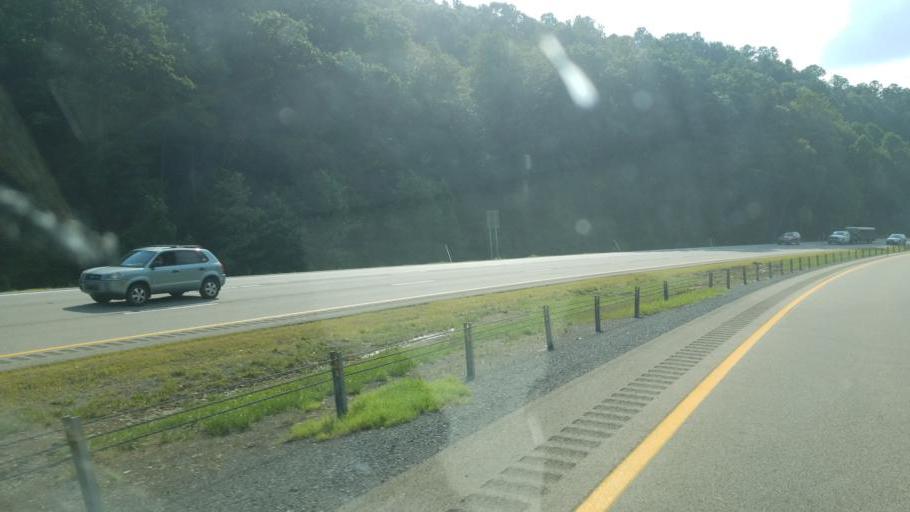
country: US
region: West Virginia
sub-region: Monongalia County
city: Cheat Lake
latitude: 39.6588
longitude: -79.8121
